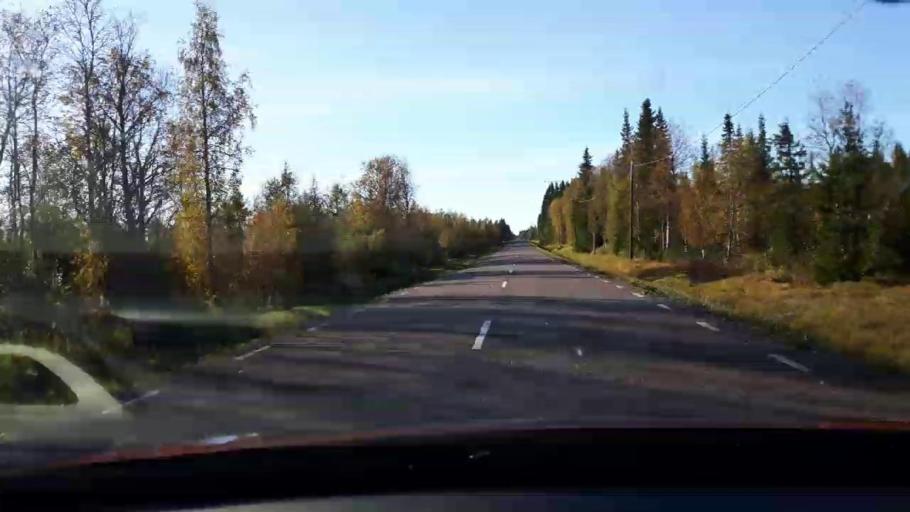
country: SE
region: Jaemtland
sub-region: Stroemsunds Kommun
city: Stroemsund
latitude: 63.8585
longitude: 15.1966
